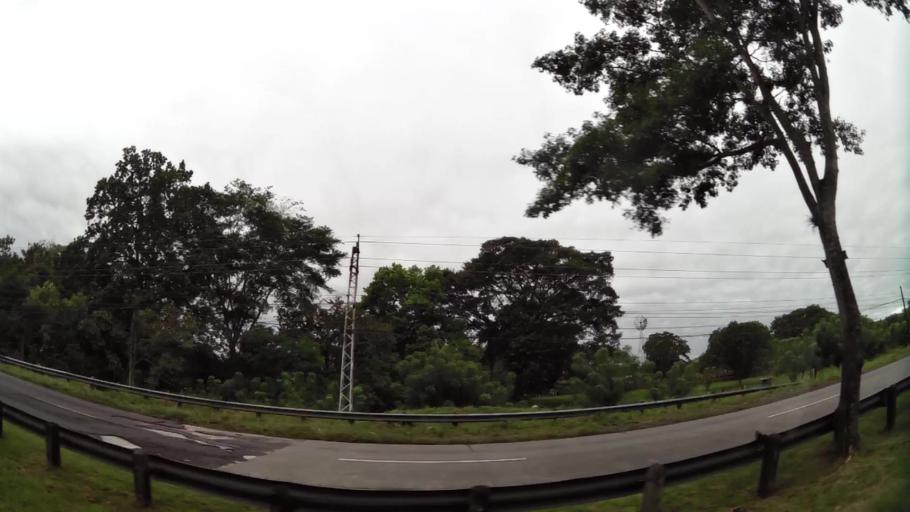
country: PA
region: Chiriqui
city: Tijera
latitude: 8.4790
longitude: -82.5538
